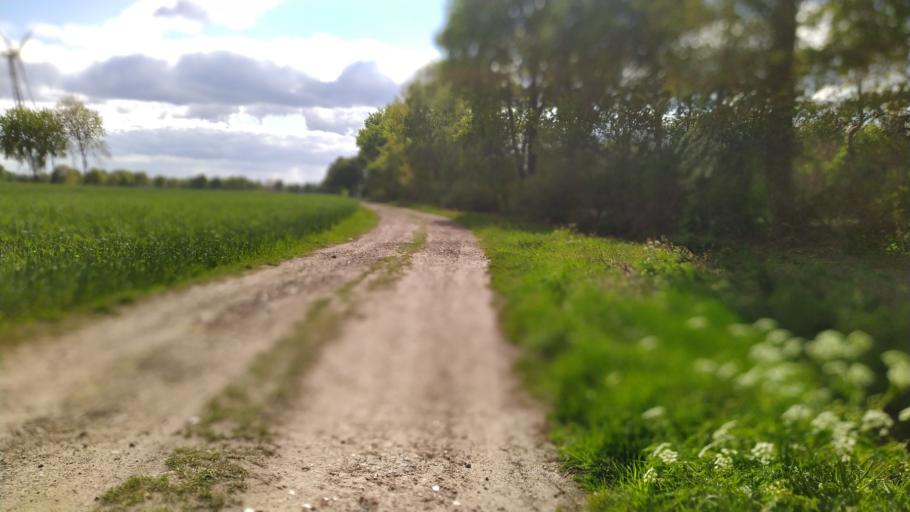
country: DE
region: Lower Saxony
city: Brest
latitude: 53.4355
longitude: 9.3837
